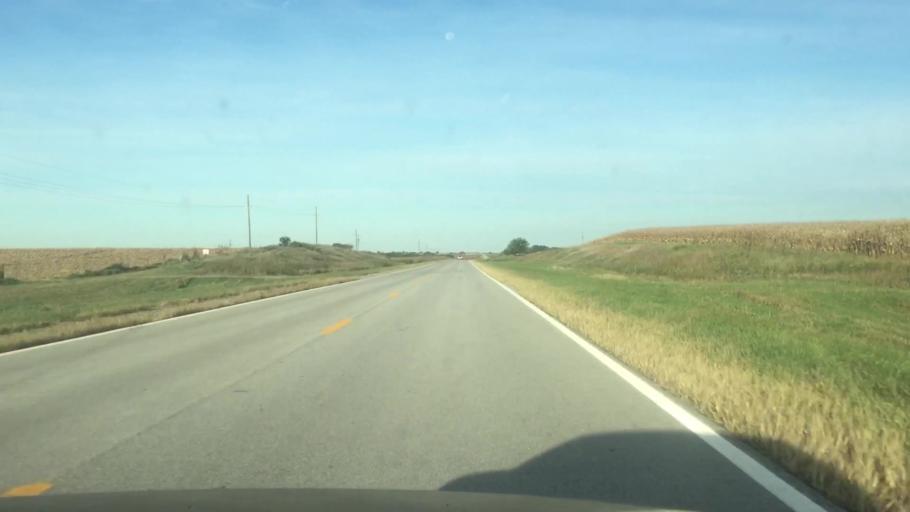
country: US
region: Nebraska
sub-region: Gage County
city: Wymore
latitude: 40.0447
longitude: -96.6671
